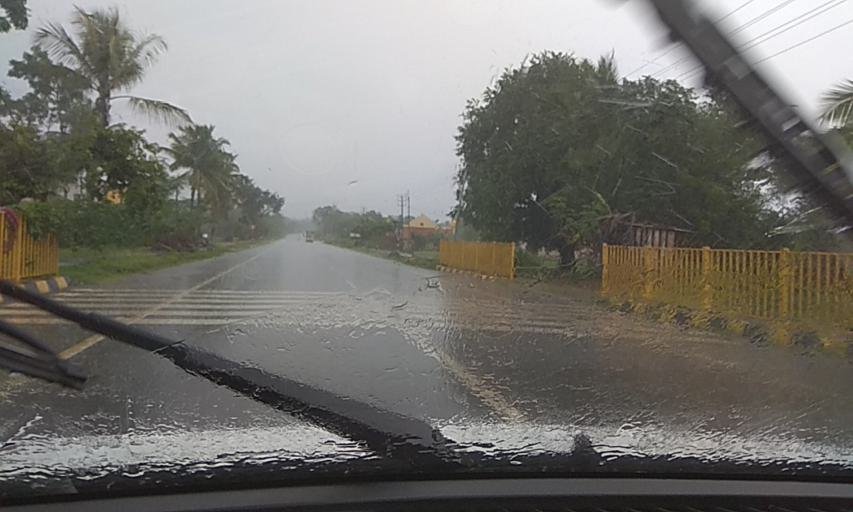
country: IN
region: Karnataka
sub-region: Mandya
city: Maddur
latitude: 12.7168
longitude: 77.0575
